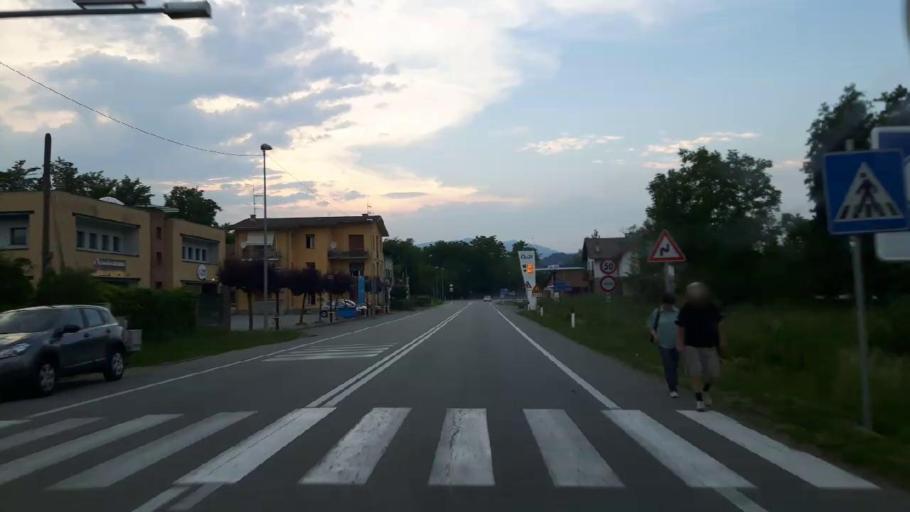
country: IT
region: Piedmont
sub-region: Provincia di Novara
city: Dormelletto
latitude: 45.7444
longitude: 8.5661
